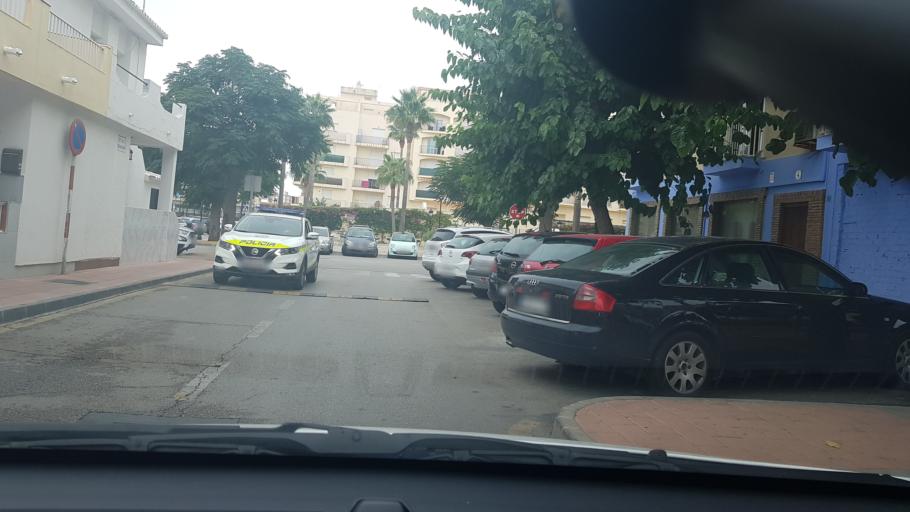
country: ES
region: Andalusia
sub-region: Provincia de Malaga
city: Manilva
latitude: 36.3655
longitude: -5.2274
